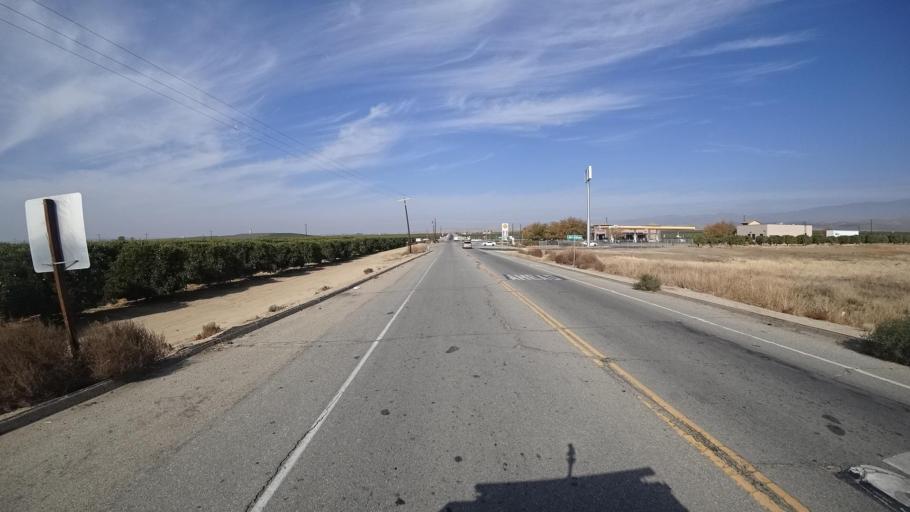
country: US
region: California
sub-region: Kern County
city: Lamont
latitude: 35.3394
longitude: -118.8432
